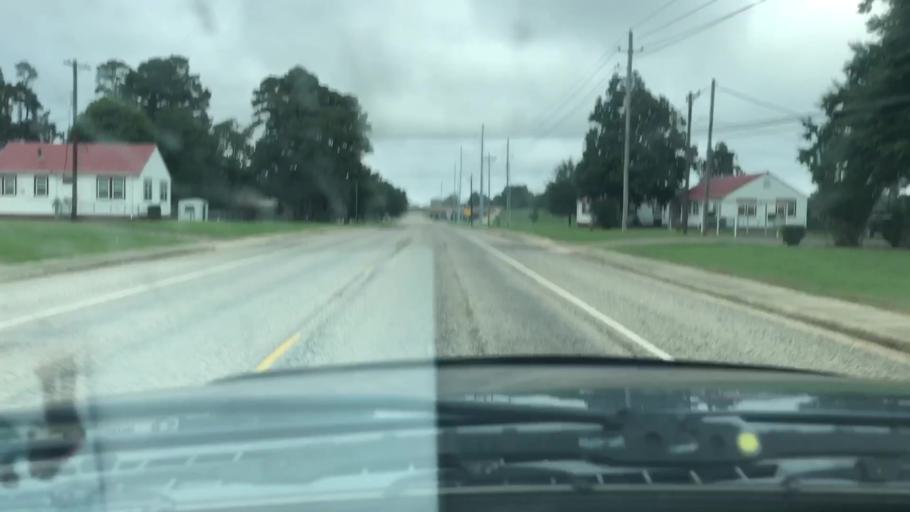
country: US
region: Texas
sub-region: Bowie County
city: Wake Village
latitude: 33.3825
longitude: -94.0921
